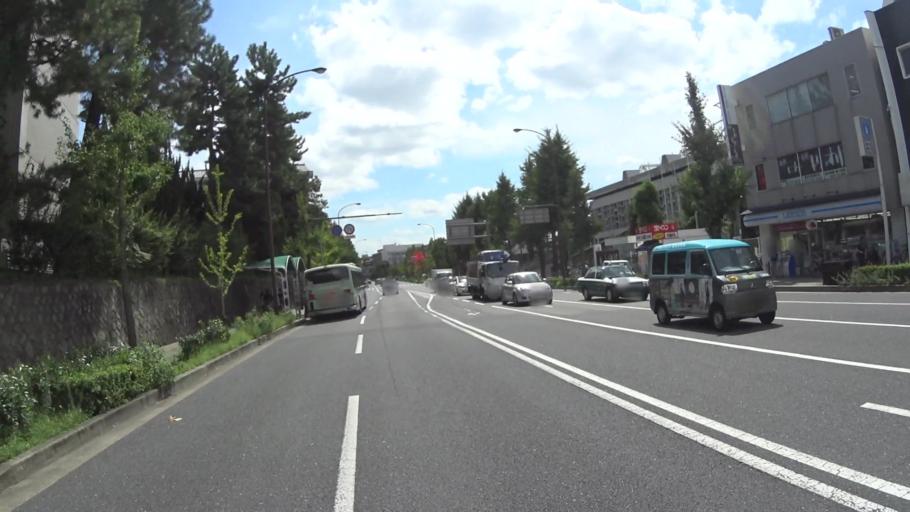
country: JP
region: Kyoto
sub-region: Kyoto-shi
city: Kamigyo-ku
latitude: 35.0286
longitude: 135.7793
